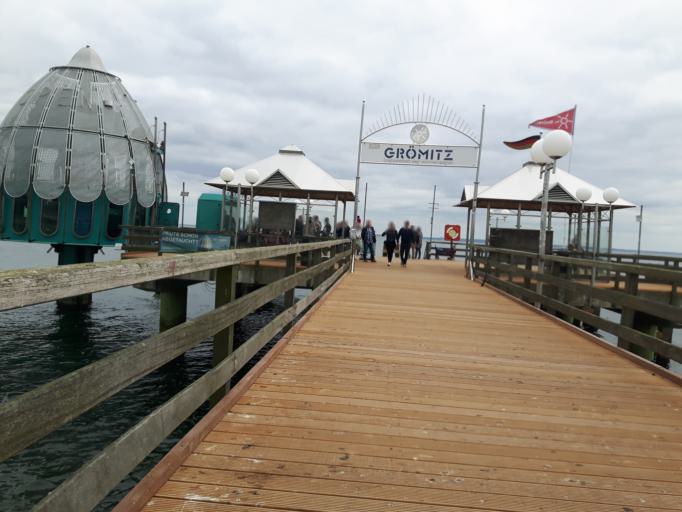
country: DE
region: Schleswig-Holstein
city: Gromitz
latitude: 54.1414
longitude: 10.9655
